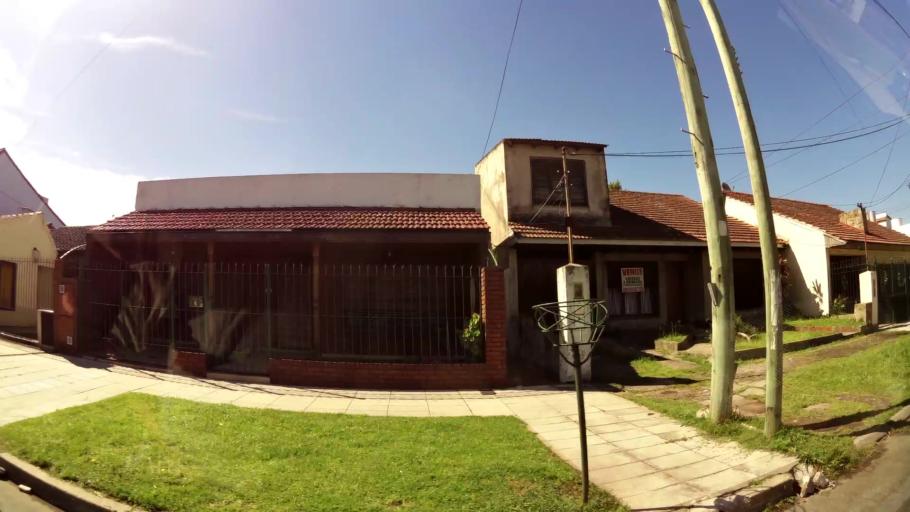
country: AR
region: Buenos Aires
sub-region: Partido de Quilmes
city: Quilmes
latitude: -34.6969
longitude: -58.3008
